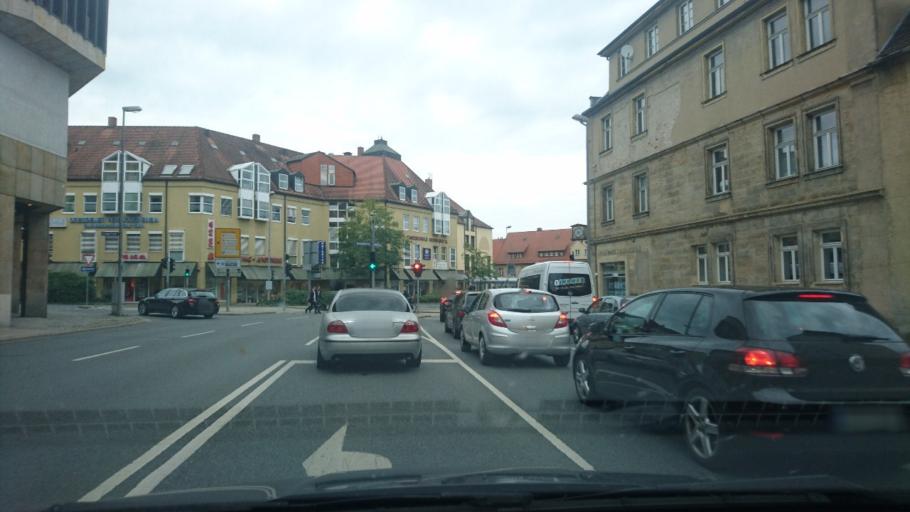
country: DE
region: Bavaria
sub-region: Upper Franconia
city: Bayreuth
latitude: 49.9433
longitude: 11.5700
